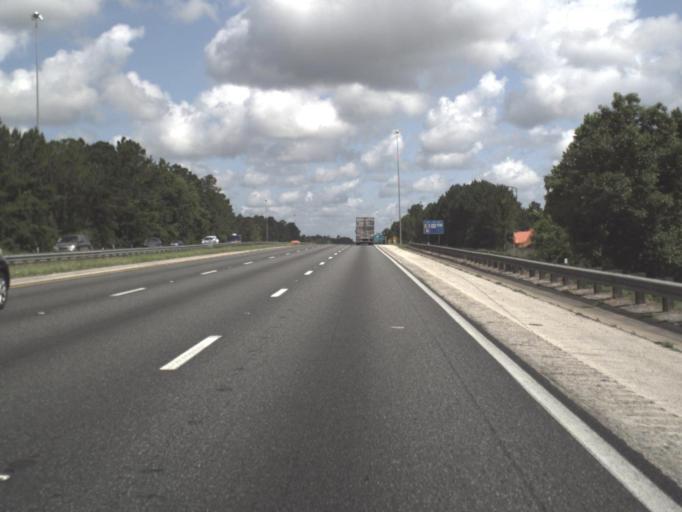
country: US
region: Florida
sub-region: Alachua County
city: Gainesville
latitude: 29.5992
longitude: -82.3706
